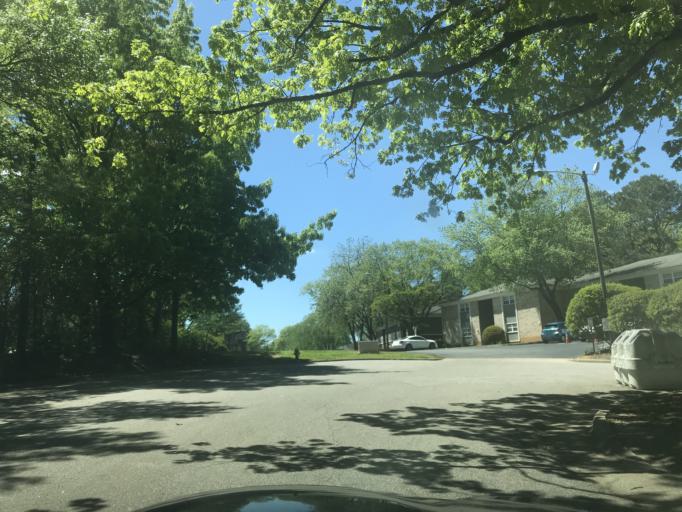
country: US
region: North Carolina
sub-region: Wake County
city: Raleigh
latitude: 35.8452
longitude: -78.5756
